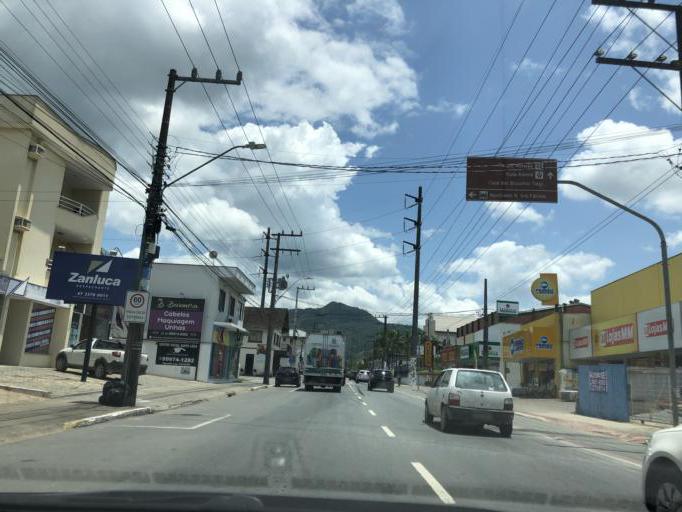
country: BR
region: Santa Catarina
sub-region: Jaragua Do Sul
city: Jaragua do Sul
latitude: -26.5126
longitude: -49.1200
